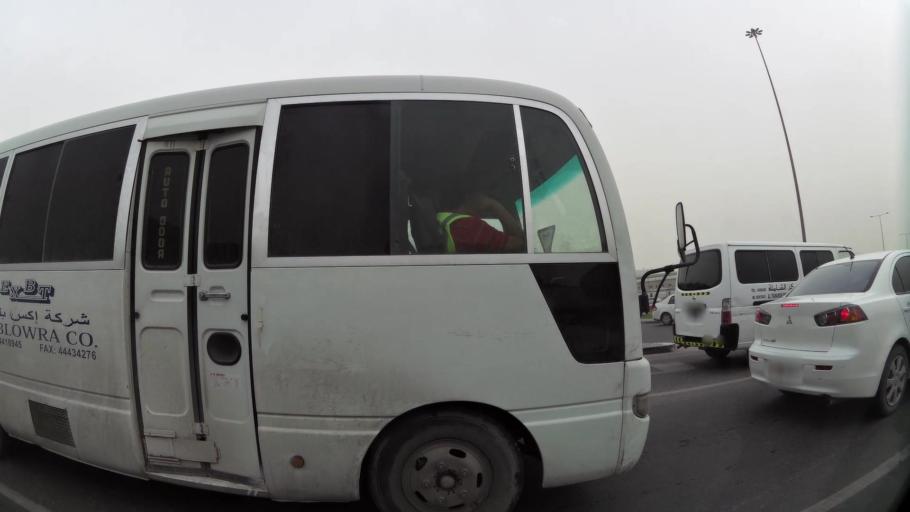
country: QA
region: Baladiyat ad Dawhah
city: Doha
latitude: 25.2443
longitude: 51.4755
